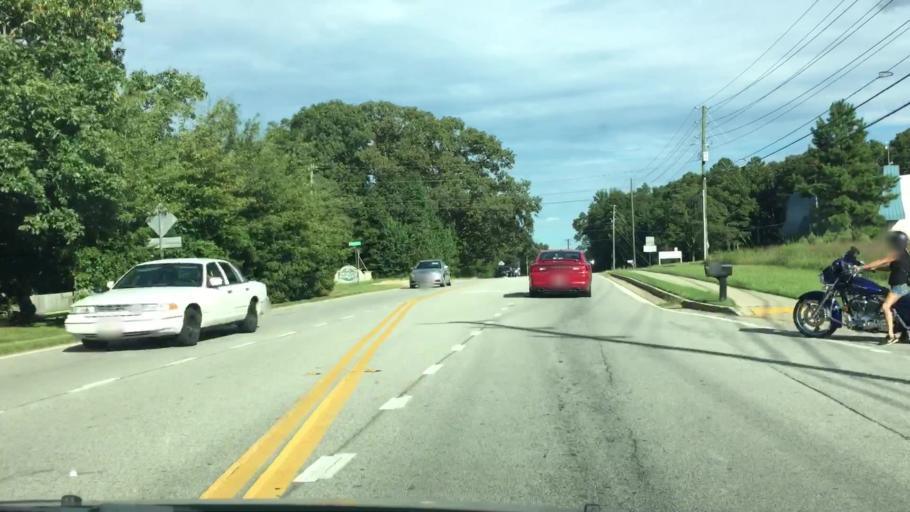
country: US
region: Georgia
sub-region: Henry County
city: Stockbridge
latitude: 33.6078
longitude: -84.2235
